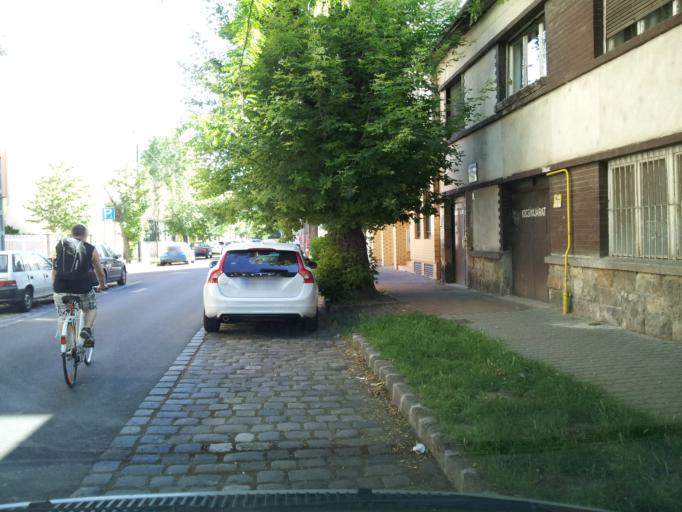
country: HU
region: Budapest
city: Budapest XIII. keruelet
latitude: 47.5337
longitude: 19.0858
